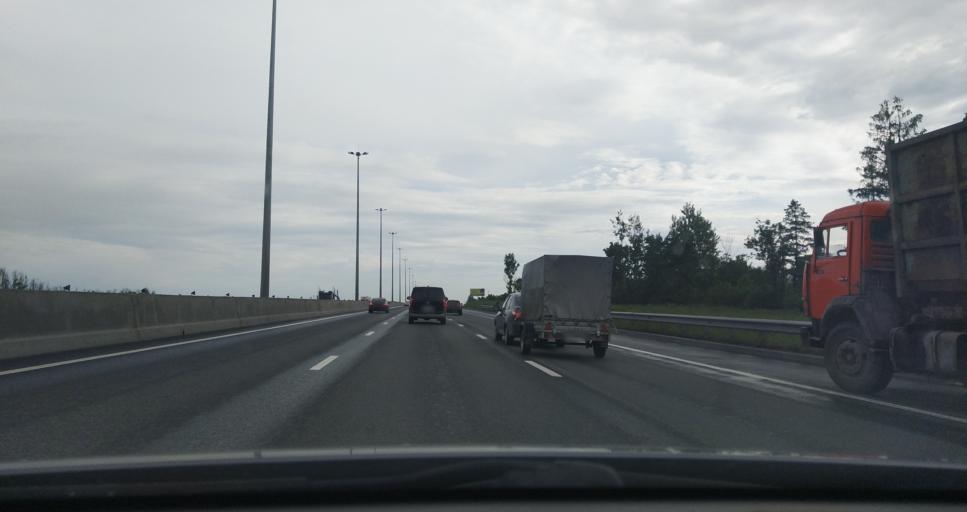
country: RU
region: St.-Petersburg
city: Aleksandrovskaya
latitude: 59.7249
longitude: 30.2893
